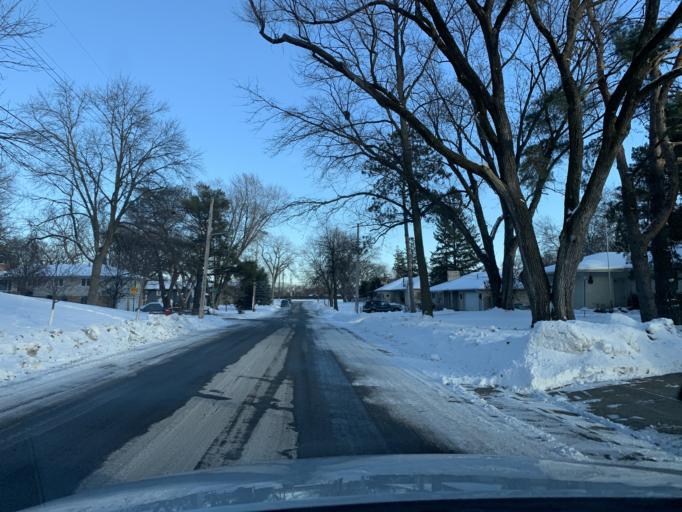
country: US
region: Minnesota
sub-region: Hennepin County
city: Minnetonka Mills
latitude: 44.9644
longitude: -93.3985
